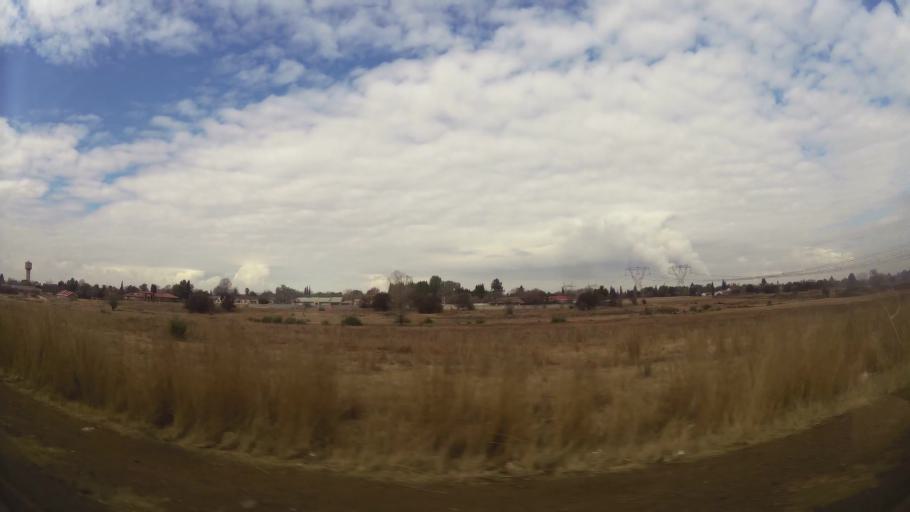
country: ZA
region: Gauteng
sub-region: Sedibeng District Municipality
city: Vereeniging
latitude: -26.6515
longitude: 28.0072
